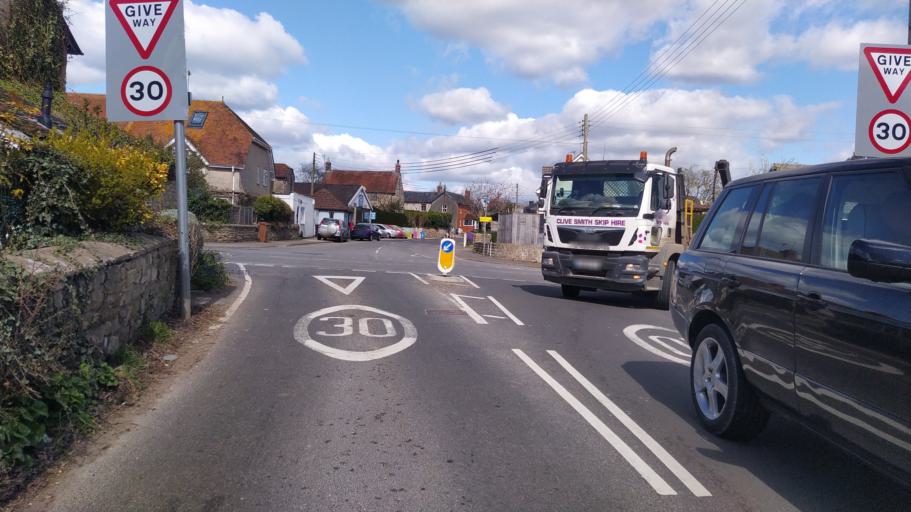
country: GB
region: England
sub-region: Dorset
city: Gillingham
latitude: 51.0051
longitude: -2.2872
